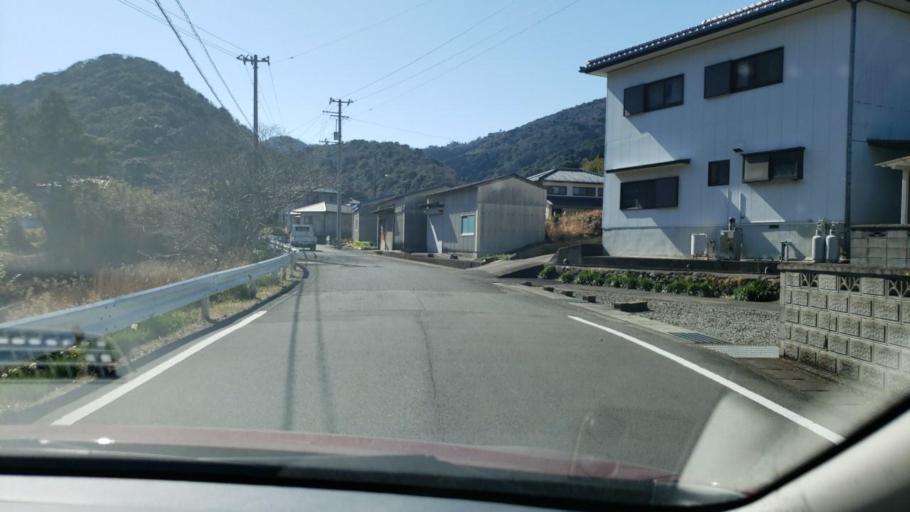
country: JP
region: Tokushima
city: Narutocho-mitsuishi
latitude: 34.2103
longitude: 134.5569
